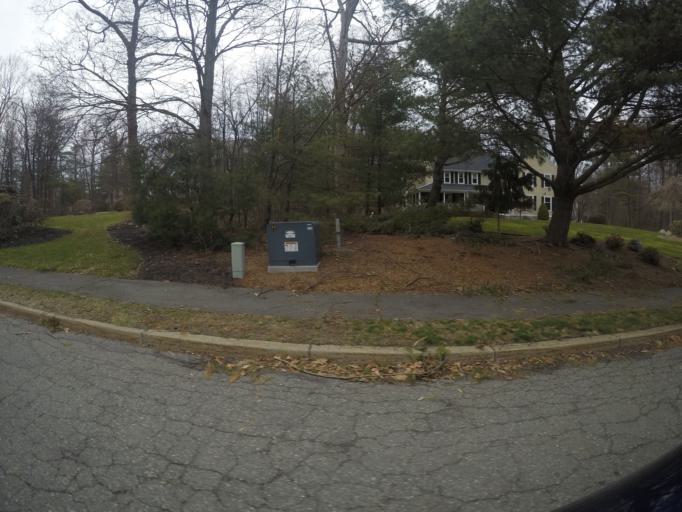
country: US
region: Massachusetts
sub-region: Norfolk County
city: Stoughton
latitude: 42.0781
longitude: -71.1052
